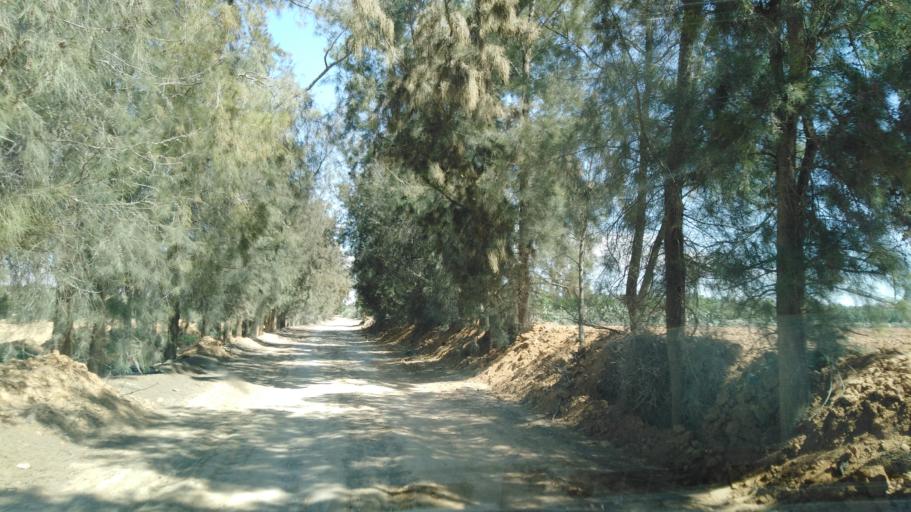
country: TN
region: Safaqis
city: Sfax
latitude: 34.7629
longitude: 10.5284
